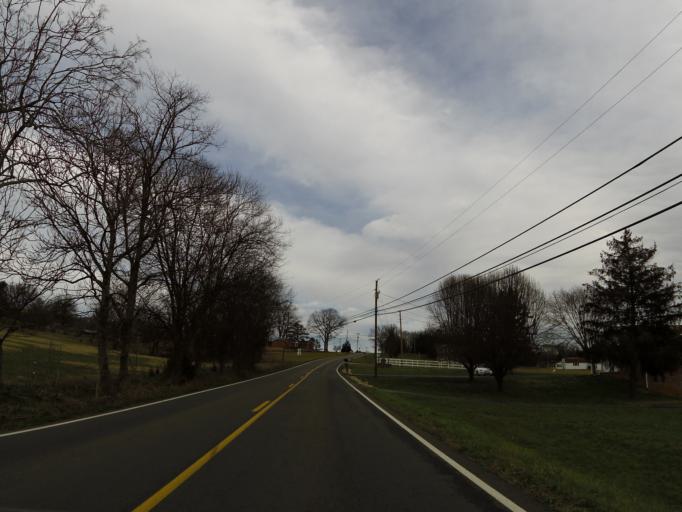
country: US
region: Tennessee
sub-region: Greene County
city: Mosheim
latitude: 36.0949
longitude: -82.9373
